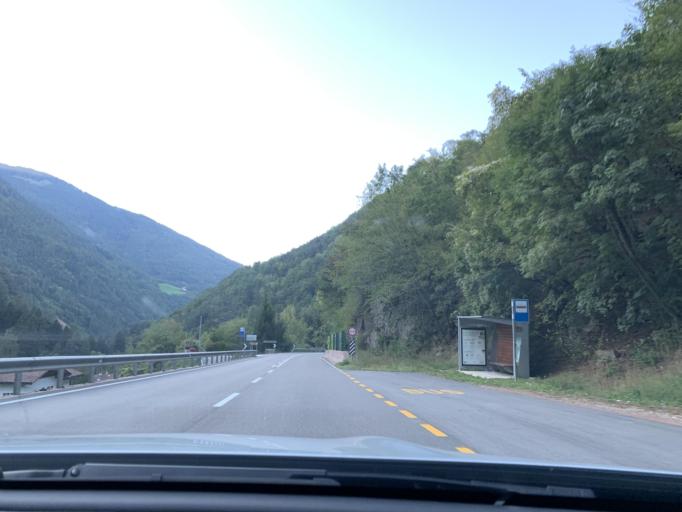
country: IT
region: Trentino-Alto Adige
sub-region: Bolzano
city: Cornedo All'Isarco
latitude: 46.4564
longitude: 11.4283
